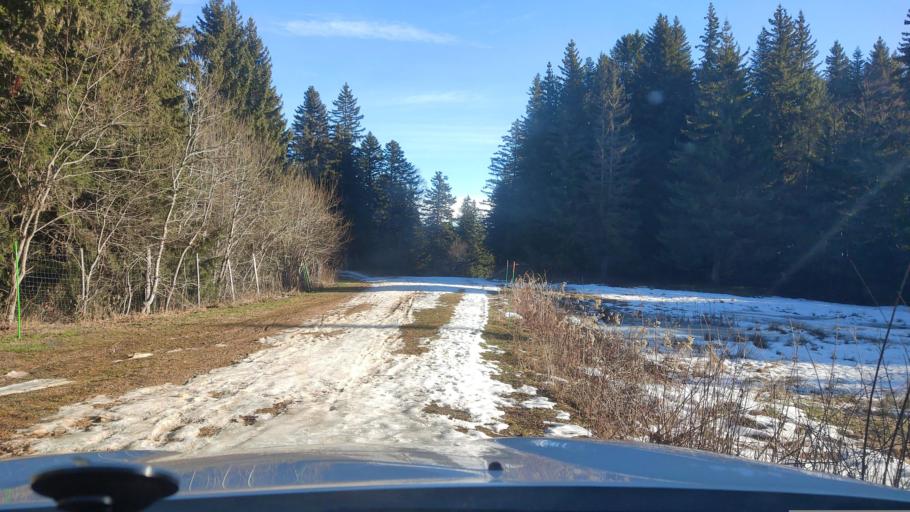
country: FR
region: Rhone-Alpes
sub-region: Departement de la Savoie
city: Mery
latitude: 45.6507
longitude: 5.9759
